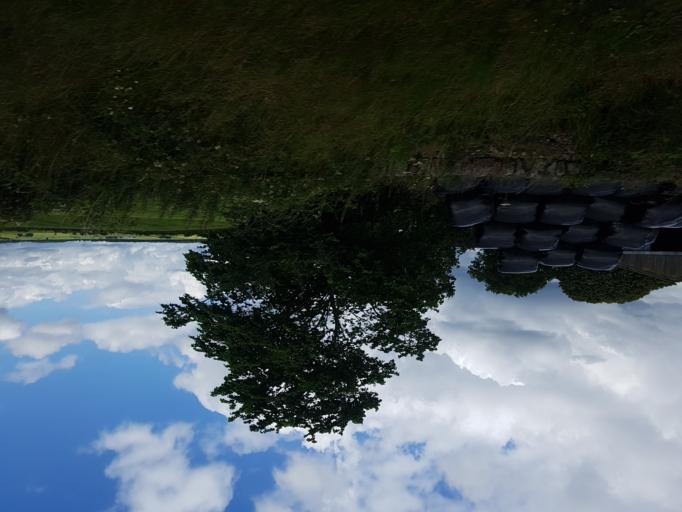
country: GB
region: Scotland
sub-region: West Lothian
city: Linlithgow
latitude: 55.9754
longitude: -3.6412
